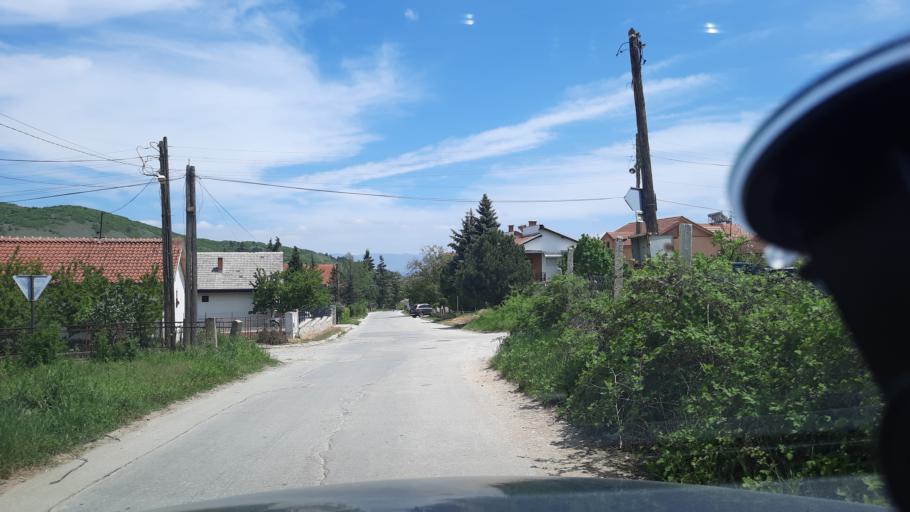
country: MK
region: Bitola
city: Bitola
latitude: 41.0325
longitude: 21.2965
